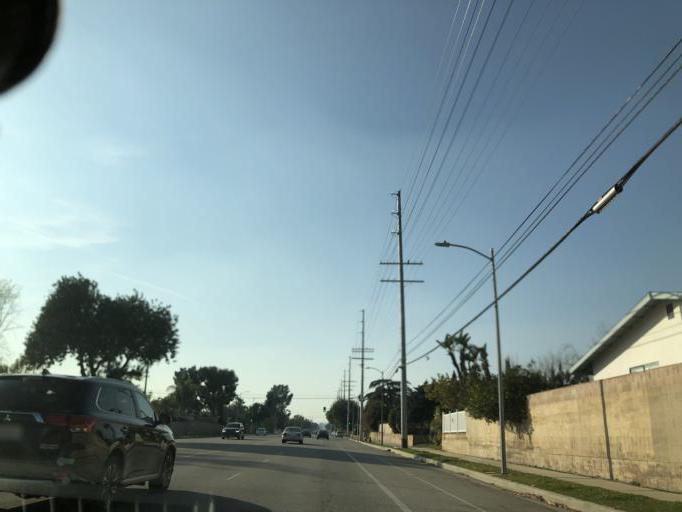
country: US
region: California
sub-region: Los Angeles County
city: San Fernando
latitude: 34.2793
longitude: -118.4874
